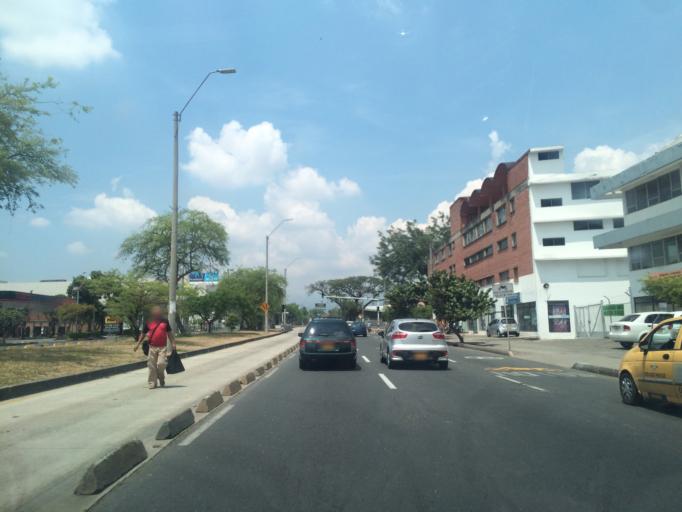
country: CO
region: Valle del Cauca
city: Cali
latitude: 3.4677
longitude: -76.5123
